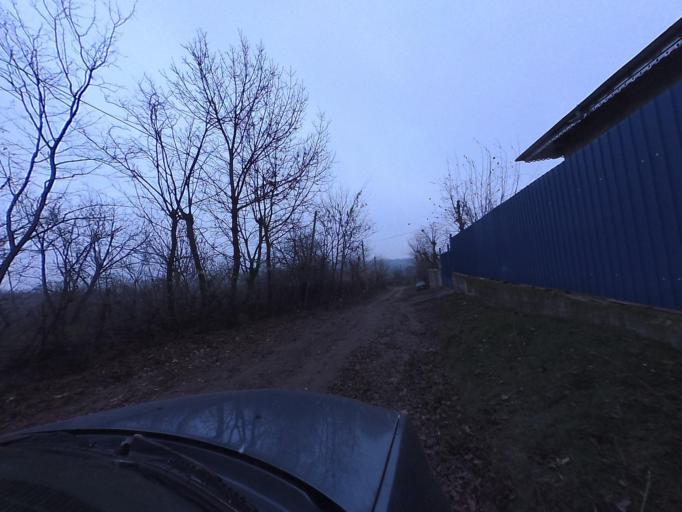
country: RO
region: Galati
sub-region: Comuna Balabanesti
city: Balabanesti
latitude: 46.1440
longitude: 27.7432
